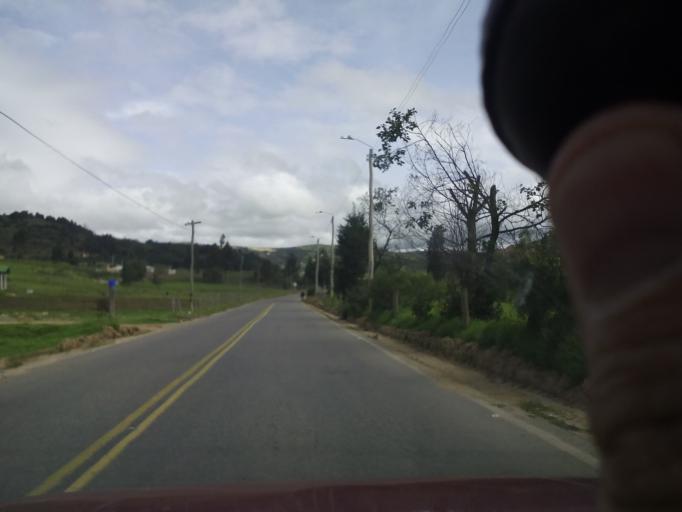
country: CO
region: Boyaca
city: Combita
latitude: 5.6243
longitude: -73.3119
